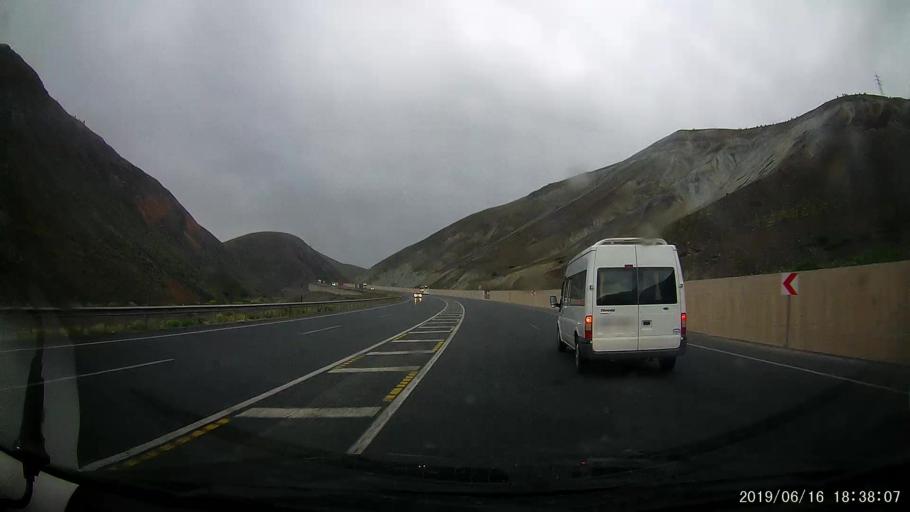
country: TR
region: Erzincan
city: Catalarmut
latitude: 39.8851
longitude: 39.1866
